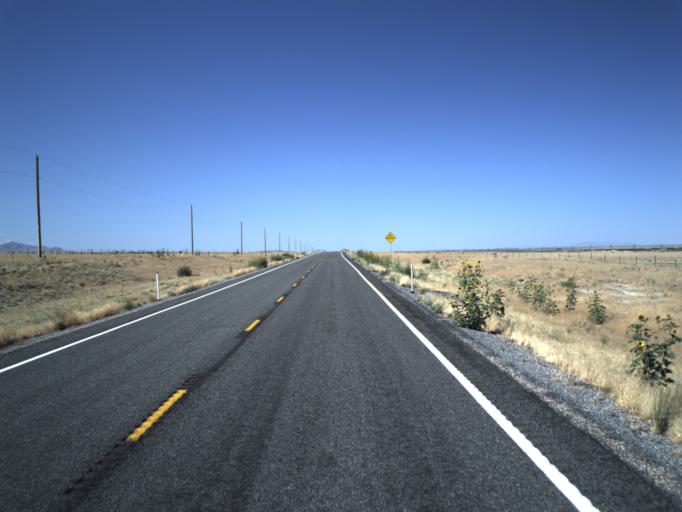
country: US
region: Utah
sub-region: Millard County
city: Delta
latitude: 39.6225
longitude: -112.3137
